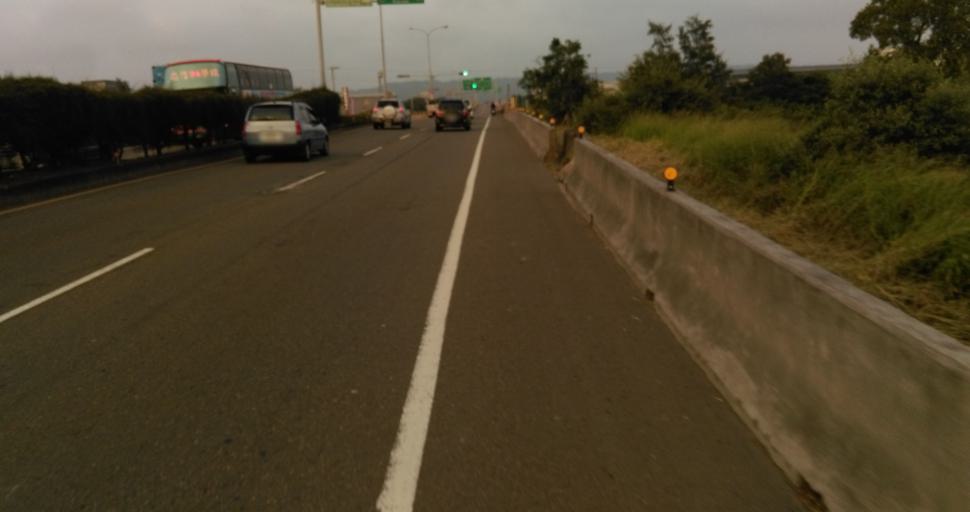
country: TW
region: Taiwan
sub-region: Hsinchu
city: Hsinchu
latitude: 24.8540
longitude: 120.9447
